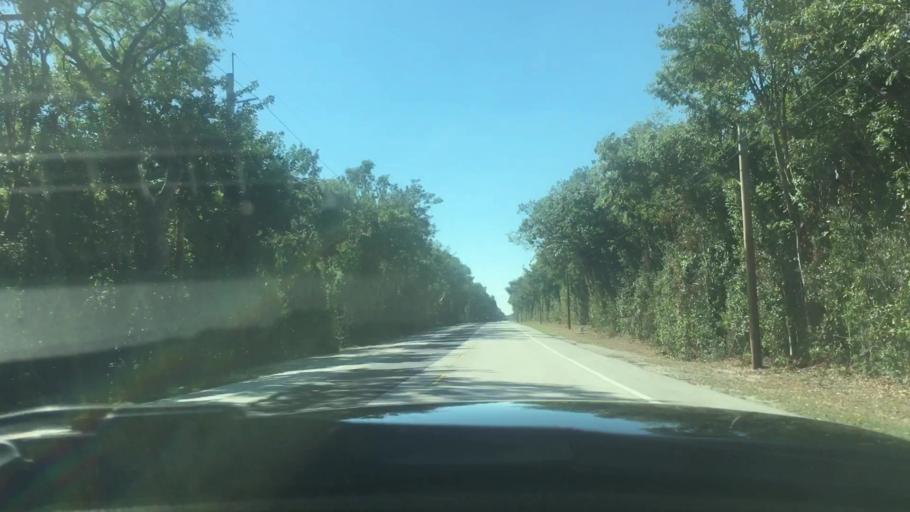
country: US
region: Florida
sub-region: Monroe County
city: North Key Largo
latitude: 25.2442
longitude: -80.3201
